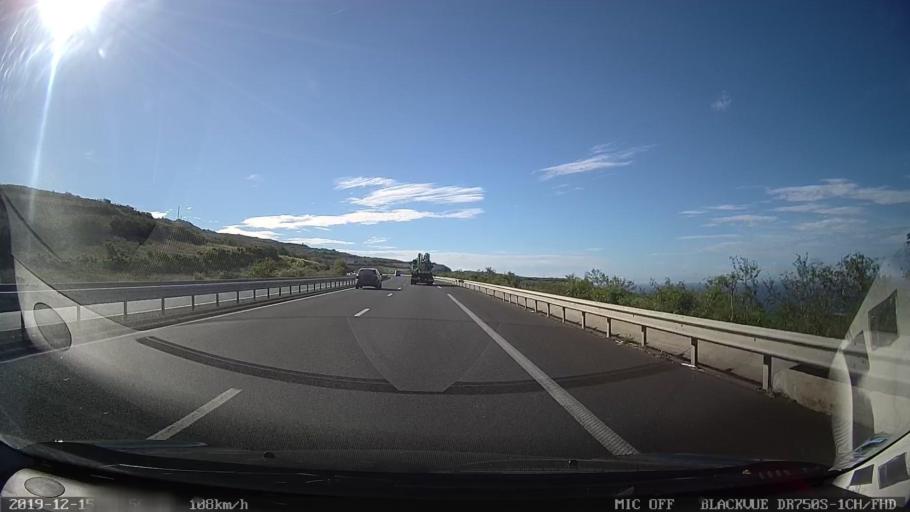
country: RE
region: Reunion
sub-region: Reunion
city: Trois-Bassins
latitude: -21.0761
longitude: 55.2520
